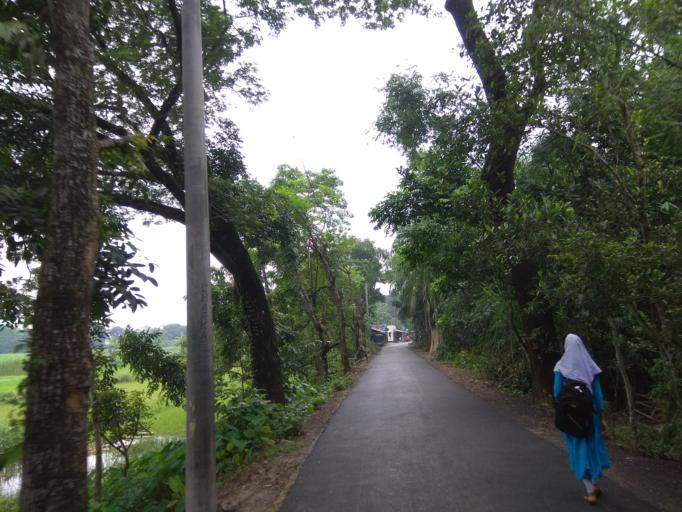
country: BD
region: Dhaka
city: Dohar
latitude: 23.4716
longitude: 90.0721
